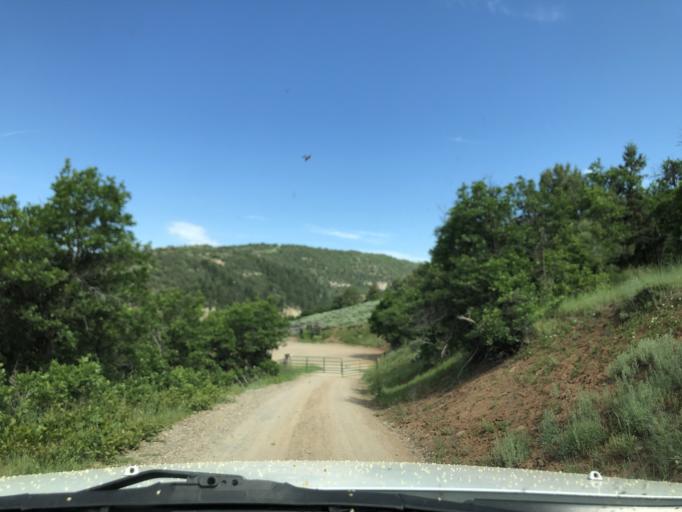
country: US
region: Colorado
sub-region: Delta County
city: Paonia
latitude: 38.9994
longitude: -107.3528
